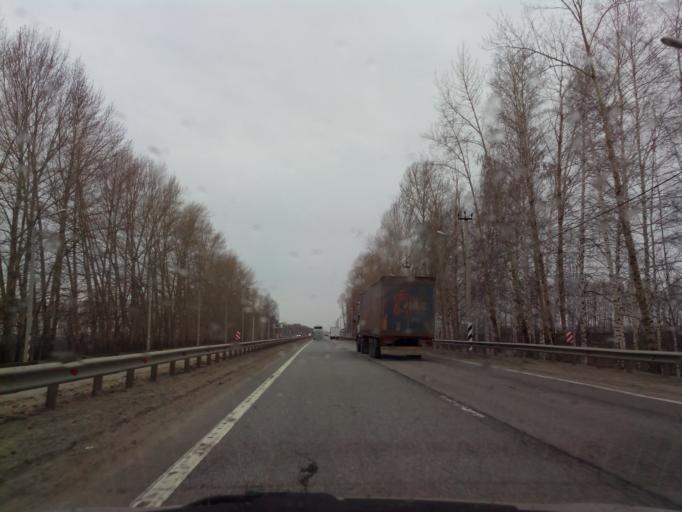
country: RU
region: Tambov
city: Selezni
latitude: 52.7556
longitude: 41.1599
